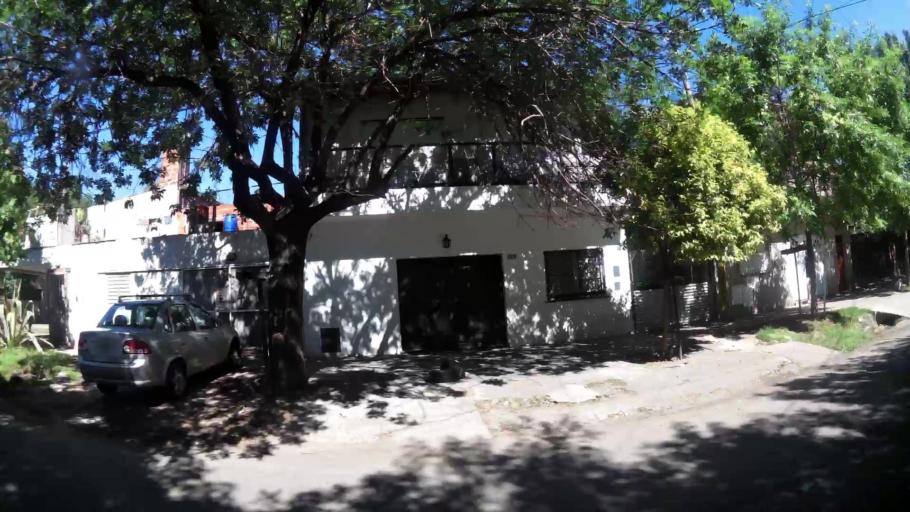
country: AR
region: Santa Fe
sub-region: Departamento de Rosario
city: Rosario
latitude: -32.9657
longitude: -60.6963
